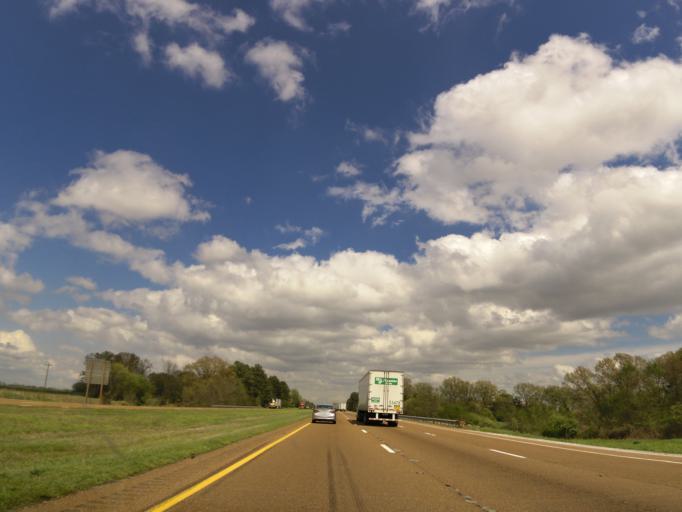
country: US
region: Tennessee
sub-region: Tipton County
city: Mason
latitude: 35.3498
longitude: -89.5162
